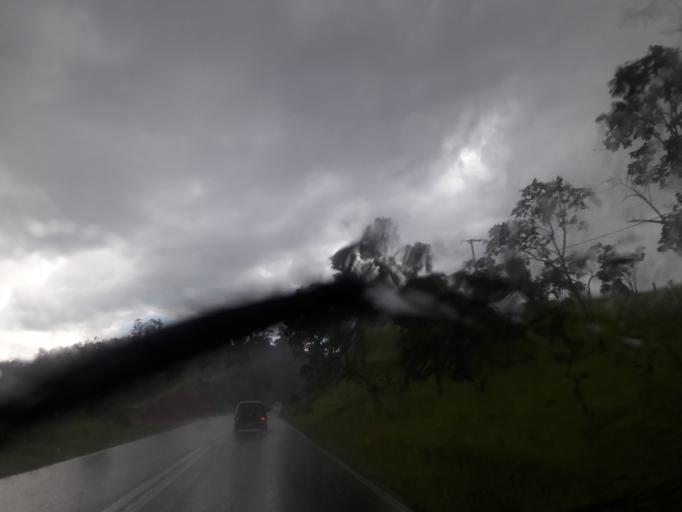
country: BR
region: Sao Paulo
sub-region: Bom Jesus Dos Perdoes
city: Bom Jesus dos Perdoes
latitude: -23.1926
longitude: -46.3973
